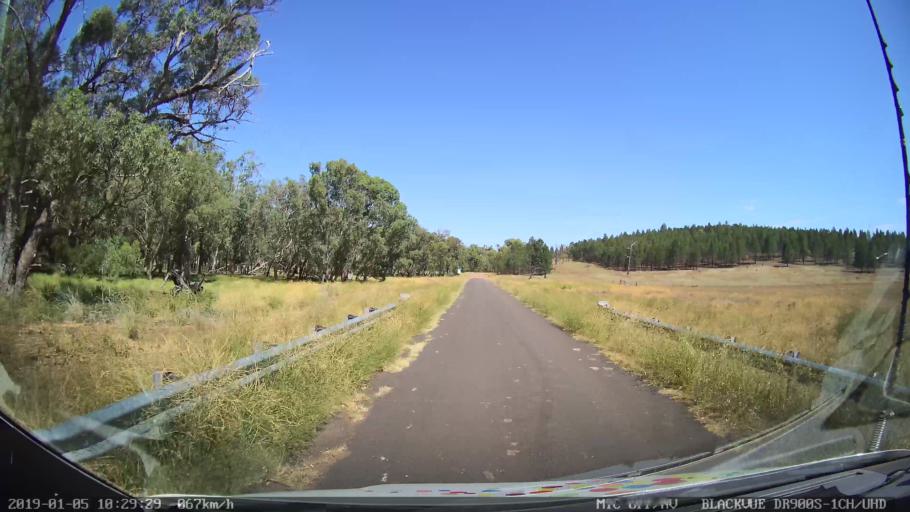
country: AU
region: New South Wales
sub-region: Gilgandra
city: Gilgandra
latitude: -31.5396
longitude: 148.9295
